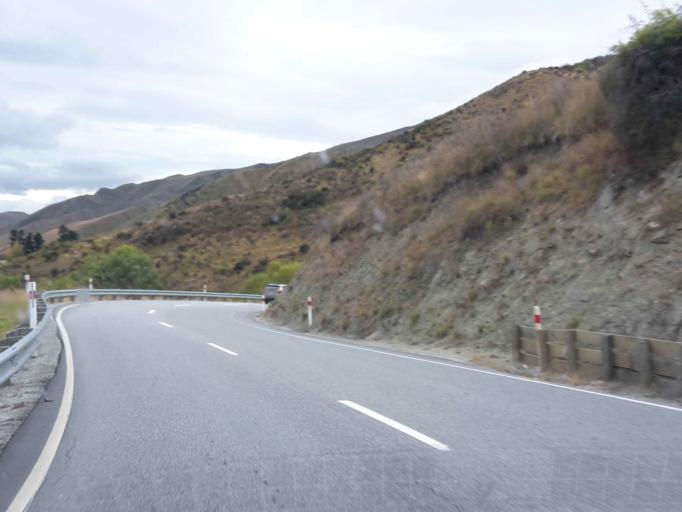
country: NZ
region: Otago
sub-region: Queenstown-Lakes District
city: Arrowtown
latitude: -44.9891
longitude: 168.9046
